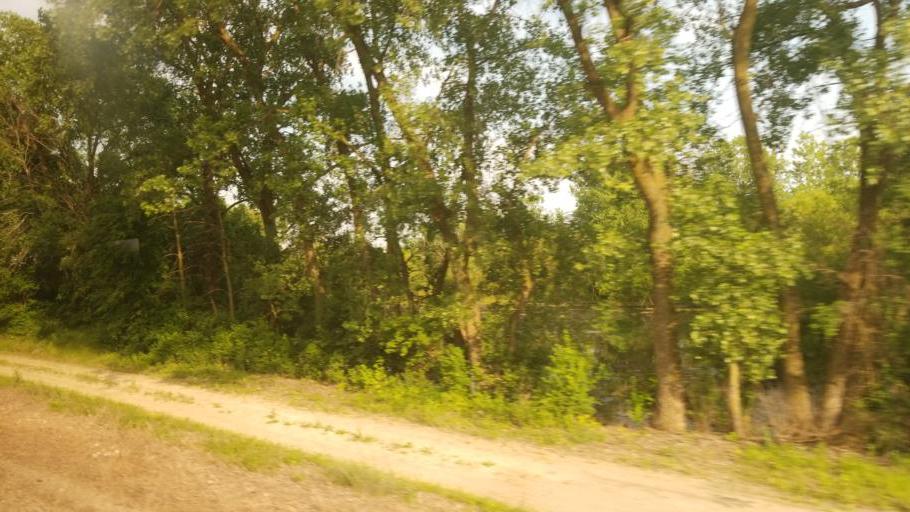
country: US
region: Illinois
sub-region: DuPage County
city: Warrenville
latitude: 41.7762
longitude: -88.2345
